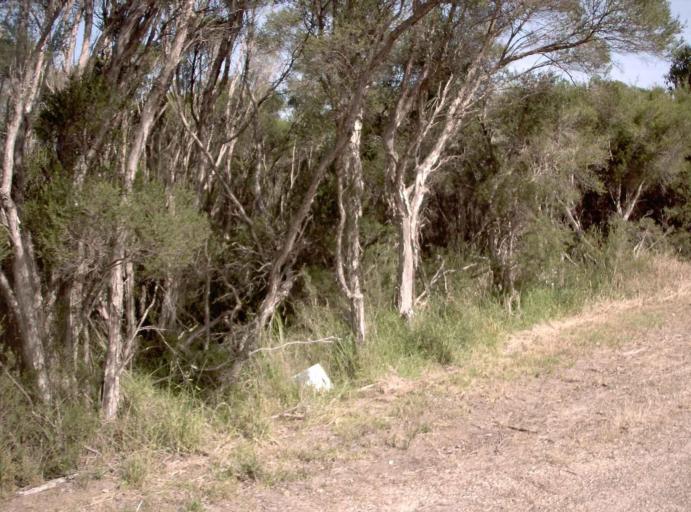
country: AU
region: Victoria
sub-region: Wellington
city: Sale
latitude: -38.2987
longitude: 147.1538
